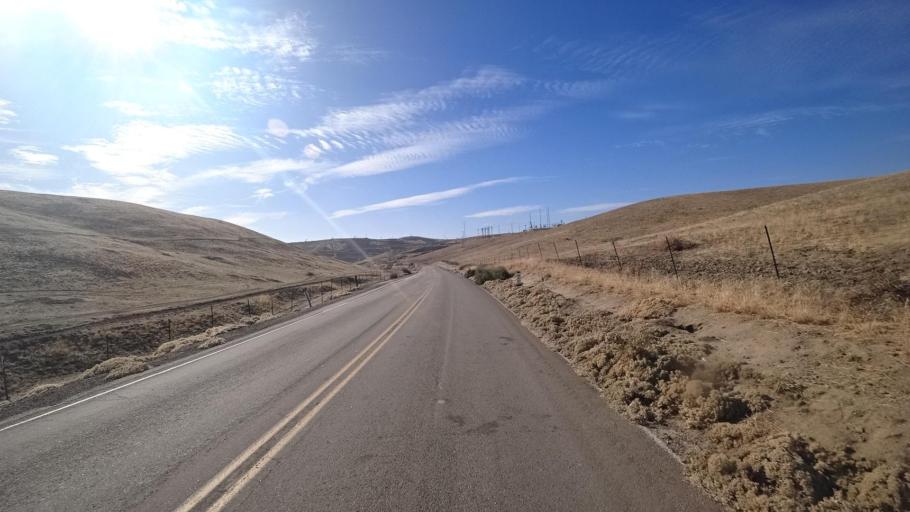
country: US
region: California
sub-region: Kern County
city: Oildale
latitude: 35.5932
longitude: -118.9545
